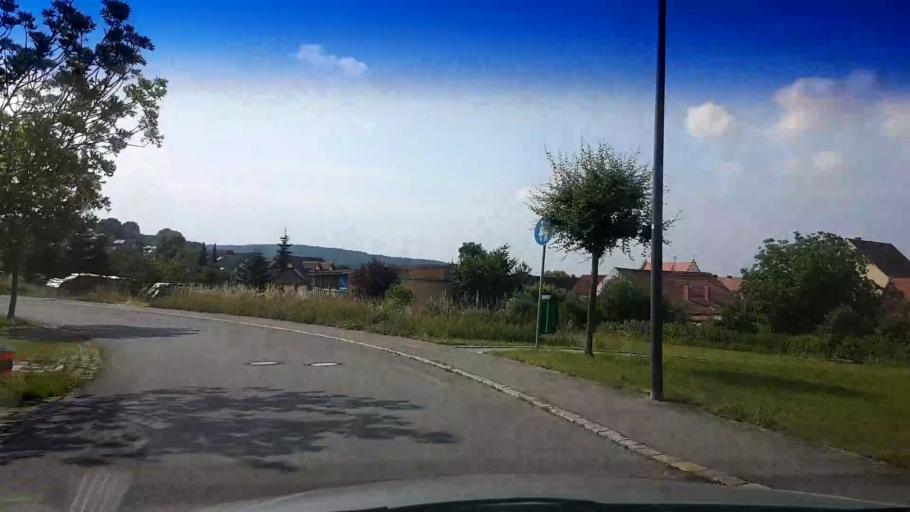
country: DE
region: Bavaria
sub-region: Upper Franconia
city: Viereth-Trunstadt
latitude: 49.9264
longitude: 10.7517
